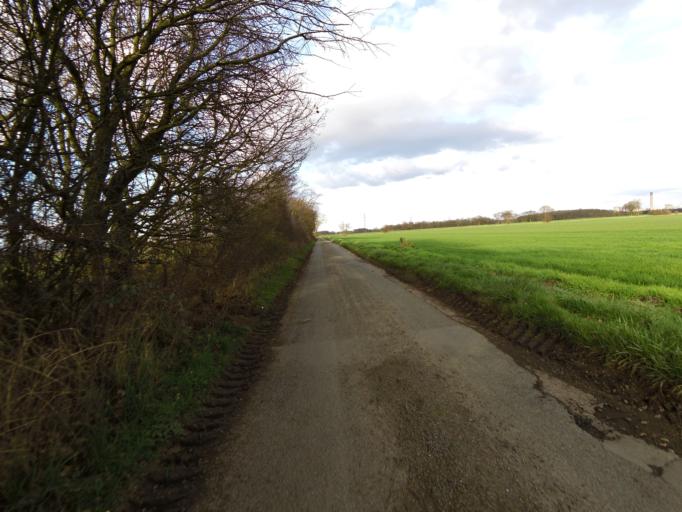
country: GB
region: England
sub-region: North Yorkshire
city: Brayton
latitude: 53.7259
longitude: -1.0750
